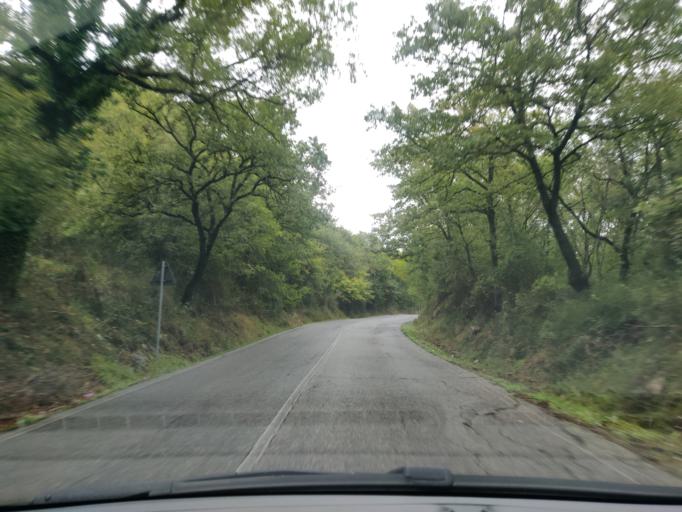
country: IT
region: Latium
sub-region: Citta metropolitana di Roma Capitale
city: Allumiere
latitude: 42.1303
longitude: 11.8668
